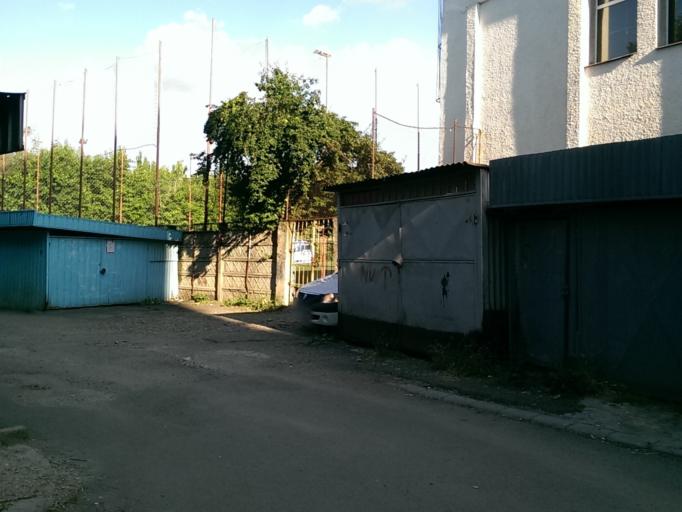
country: RO
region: Cluj
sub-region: Municipiul Cluj-Napoca
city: Cluj-Napoca
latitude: 46.7612
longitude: 23.6156
